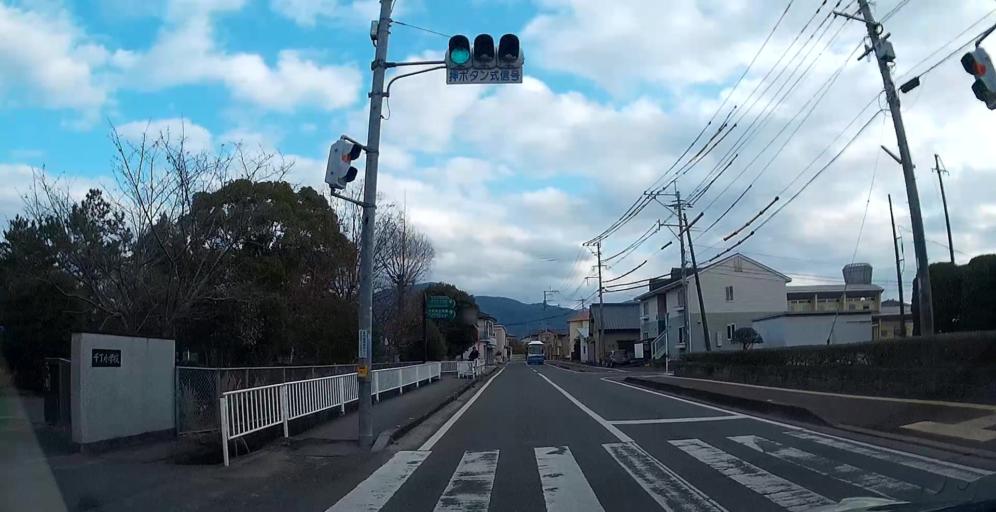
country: JP
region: Kumamoto
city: Yatsushiro
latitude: 32.5355
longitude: 130.6344
